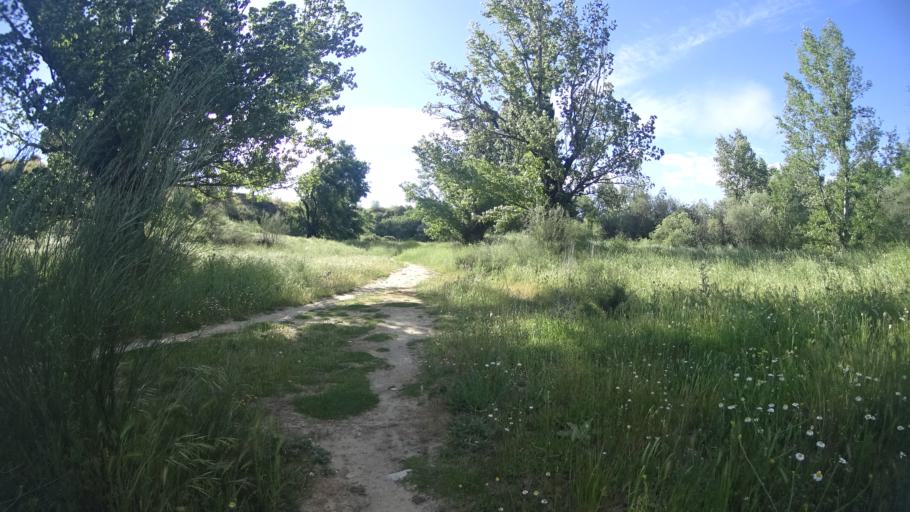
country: ES
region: Madrid
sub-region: Provincia de Madrid
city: Villanueva del Pardillo
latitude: 40.5126
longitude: -3.9383
